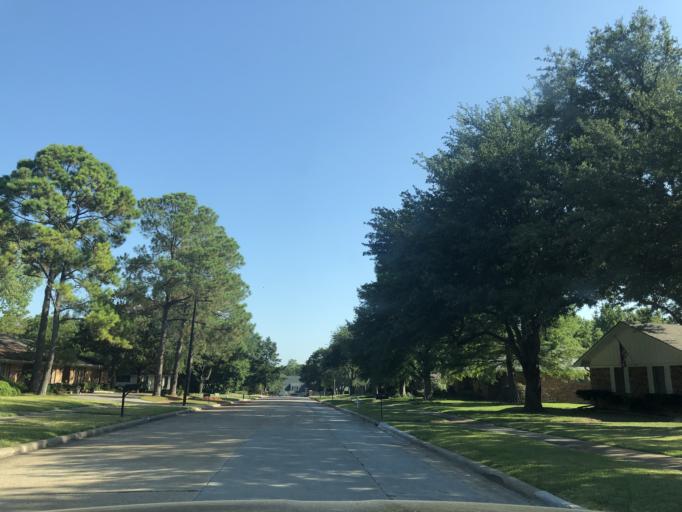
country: US
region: Texas
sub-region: Dallas County
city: Garland
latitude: 32.8691
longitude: -96.6407
